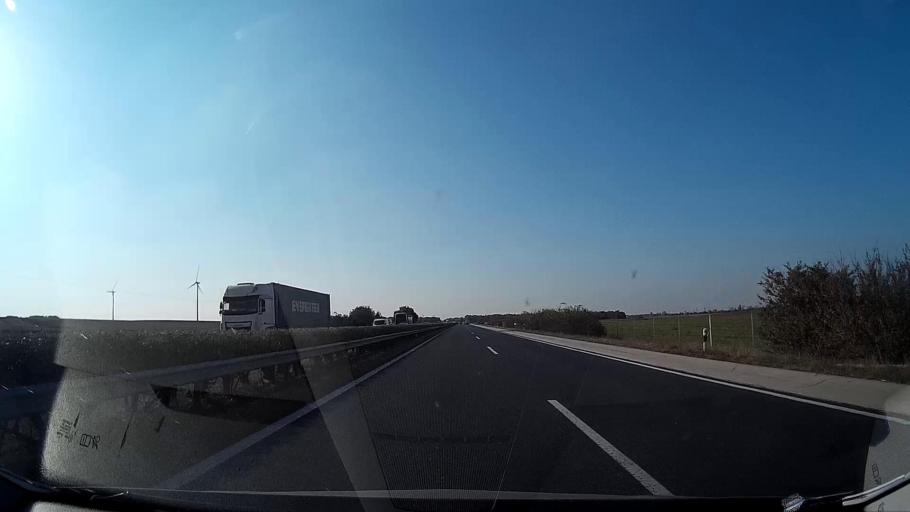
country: HU
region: Komarom-Esztergom
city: Mocsa
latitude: 47.6685
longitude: 18.1350
